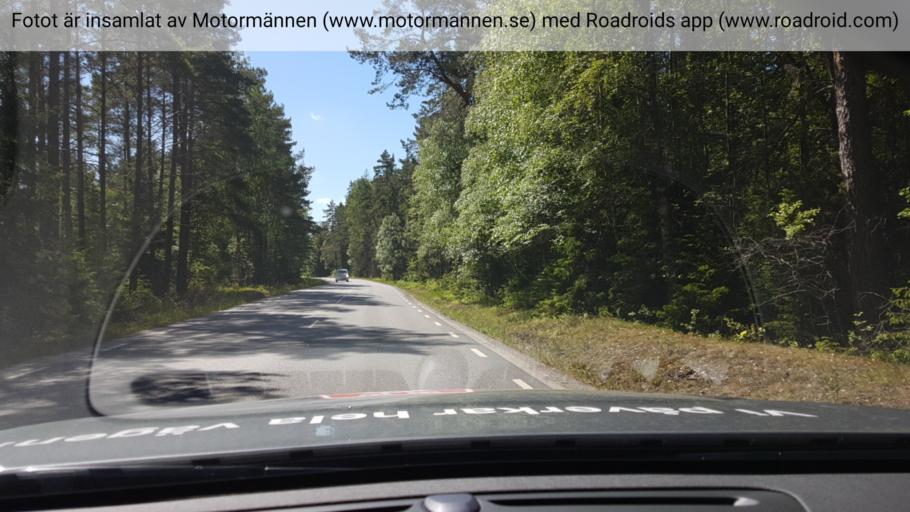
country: SE
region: Stockholm
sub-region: Haninge Kommun
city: Haninge
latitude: 59.1589
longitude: 18.1808
